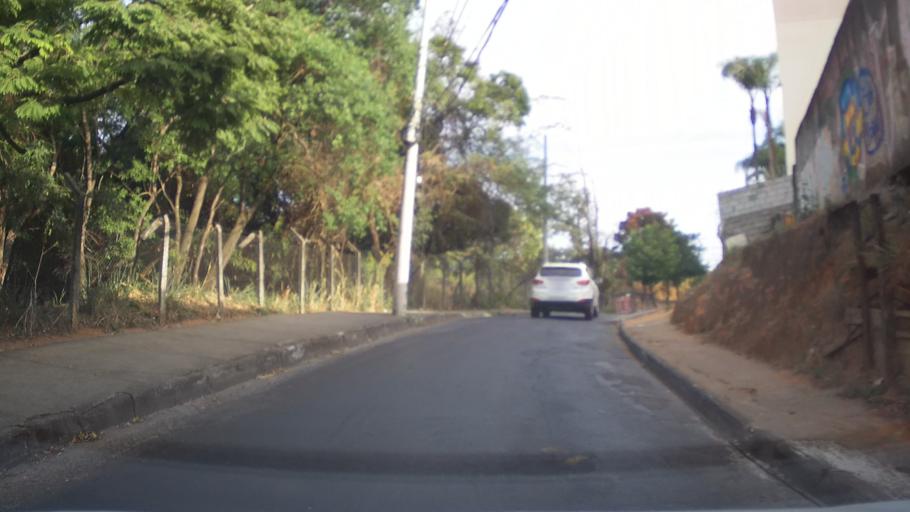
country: BR
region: Minas Gerais
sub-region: Belo Horizonte
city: Belo Horizonte
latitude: -19.8667
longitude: -43.9960
